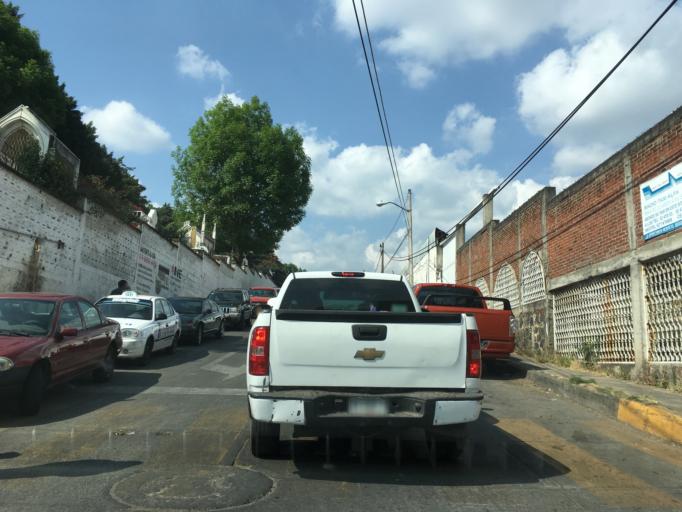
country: MX
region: Michoacan
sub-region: Uruapan
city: Uruapan
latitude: 19.4121
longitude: -102.0667
